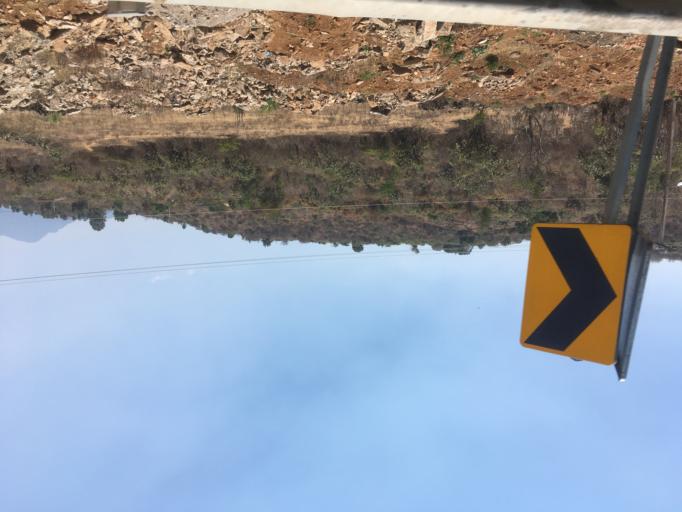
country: MX
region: Michoacan
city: Santa Fe de la Laguna
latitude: 19.6721
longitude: -101.5637
